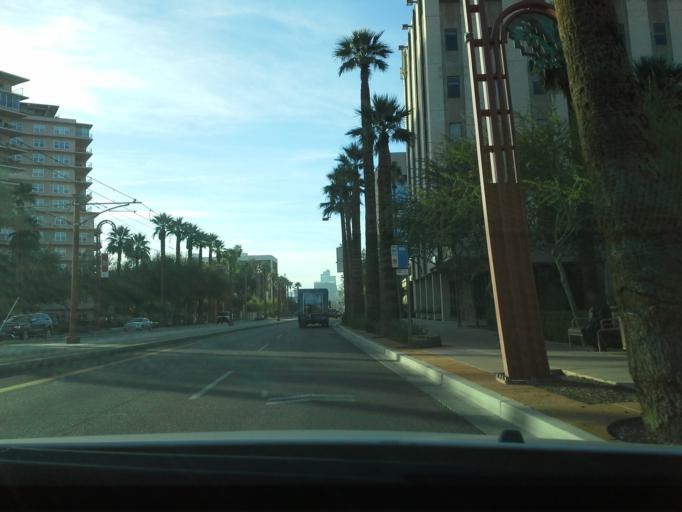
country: US
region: Arizona
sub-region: Maricopa County
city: Phoenix
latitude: 33.4727
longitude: -112.0740
